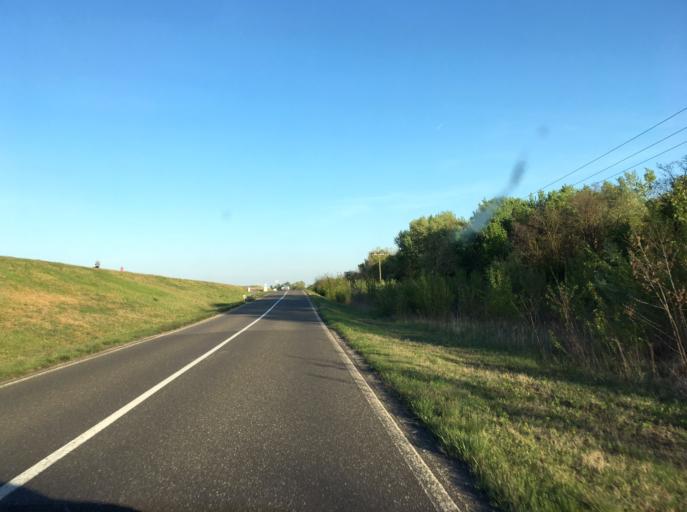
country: SK
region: Trnavsky
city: Samorin
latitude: 48.0018
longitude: 17.2589
